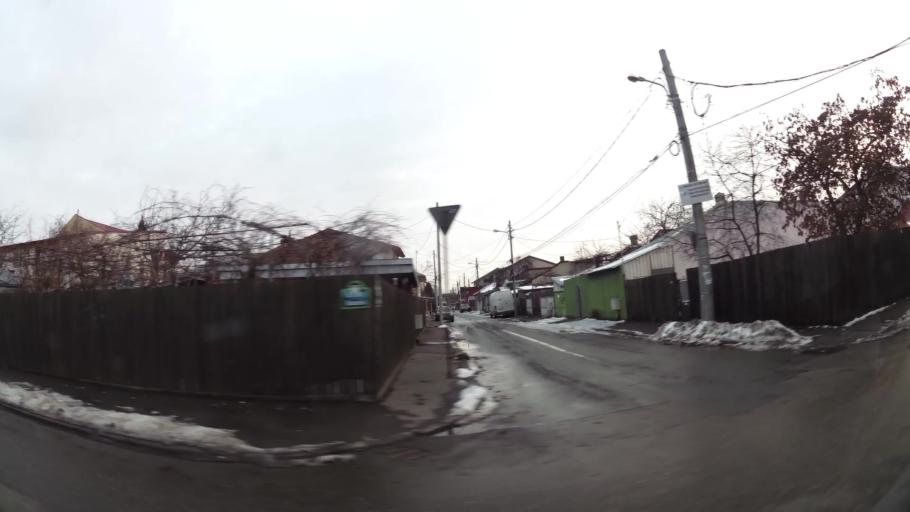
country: RO
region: Ilfov
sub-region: Comuna Fundeni-Dobroesti
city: Fundeni
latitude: 44.4738
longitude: 26.1649
